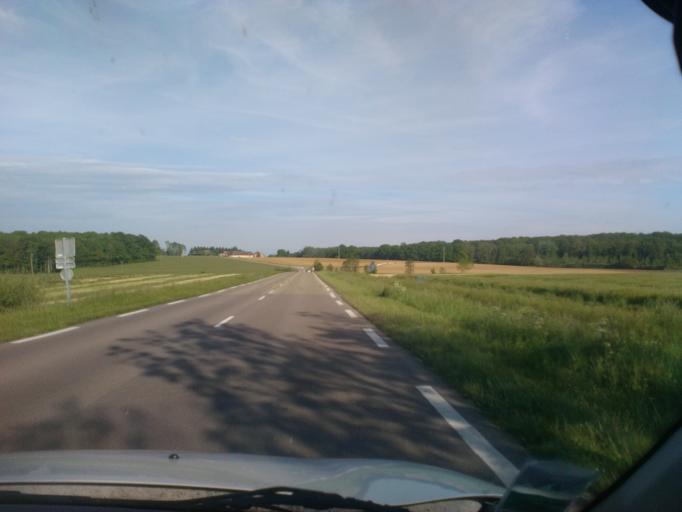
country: FR
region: Champagne-Ardenne
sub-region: Departement de l'Aube
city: Vendeuvre-sur-Barse
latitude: 48.2398
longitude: 4.3783
